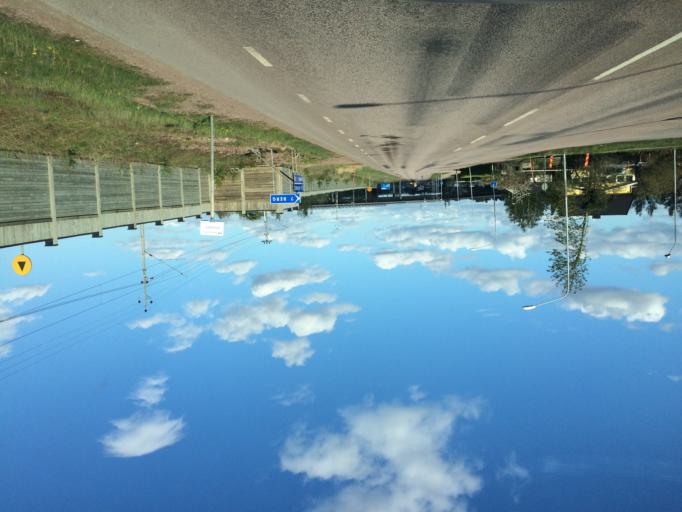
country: SE
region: Vaestmanland
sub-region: Hallstahammars Kommun
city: Kolback
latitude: 59.5589
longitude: 16.2204
